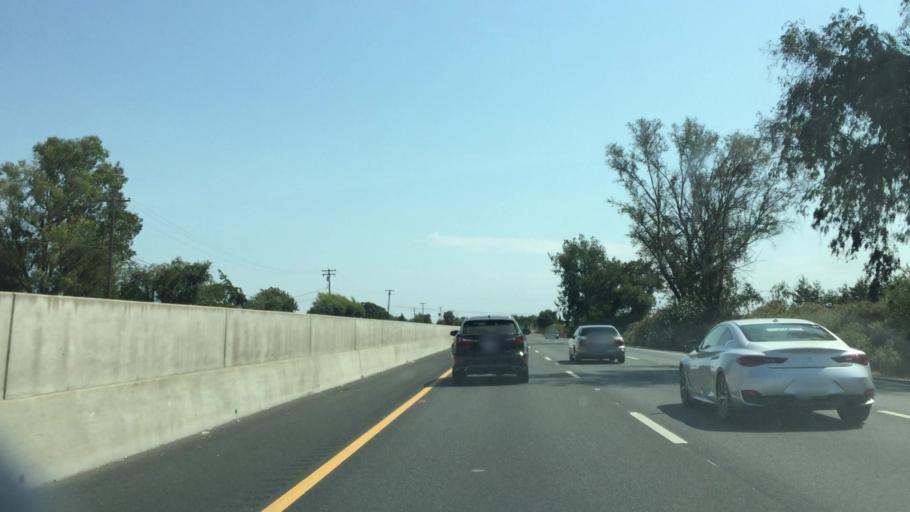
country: US
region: California
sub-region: San Joaquin County
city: Morada
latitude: 38.0656
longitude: -121.2597
